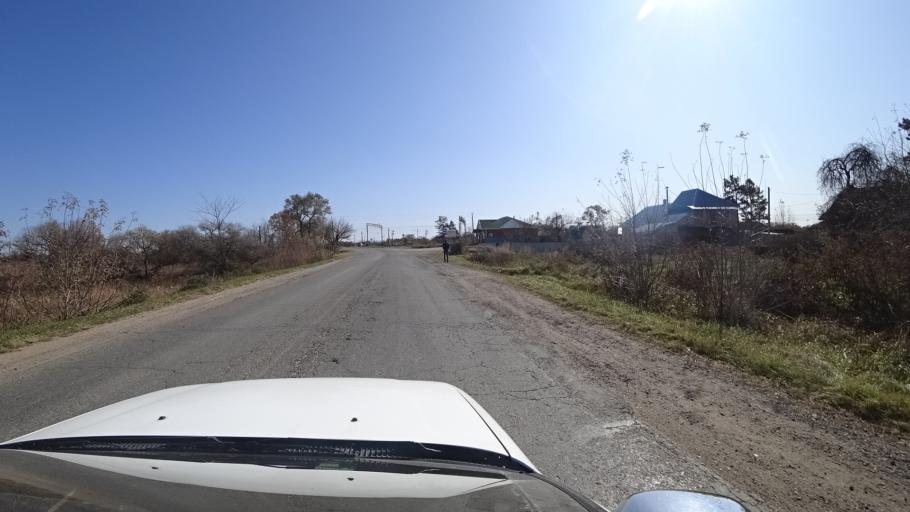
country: RU
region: Primorskiy
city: Dal'nerechensk
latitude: 45.9128
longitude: 133.7922
